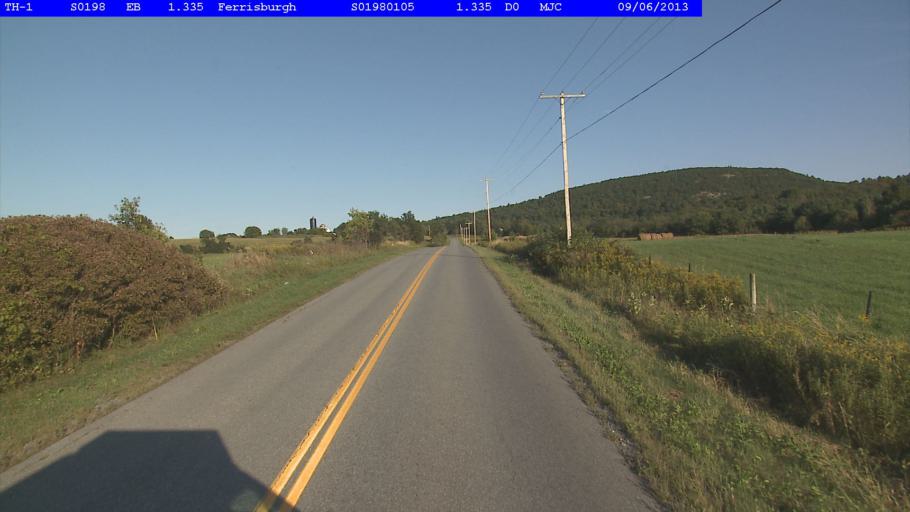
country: US
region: Vermont
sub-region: Addison County
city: Vergennes
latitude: 44.2565
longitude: -73.2022
